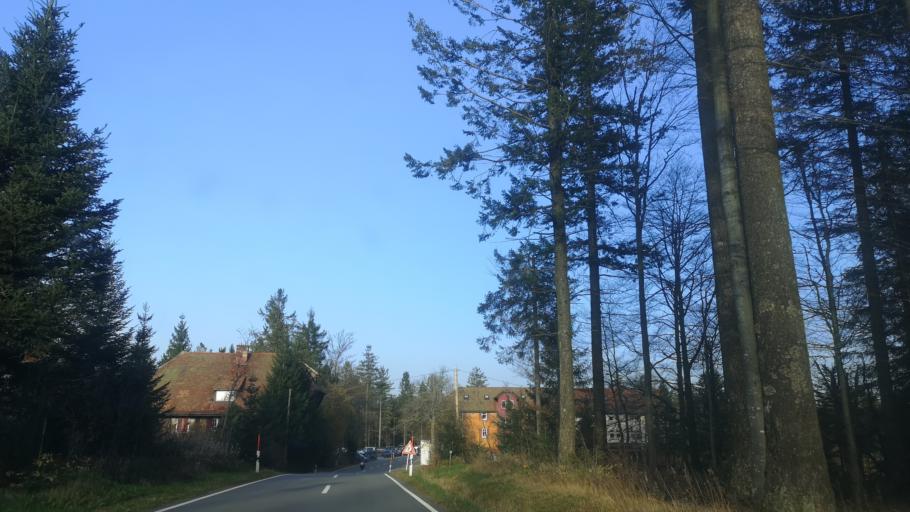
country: DE
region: Baden-Wuerttemberg
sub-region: Freiburg Region
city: Bad Peterstal-Griesbach
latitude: 48.4916
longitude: 8.2427
